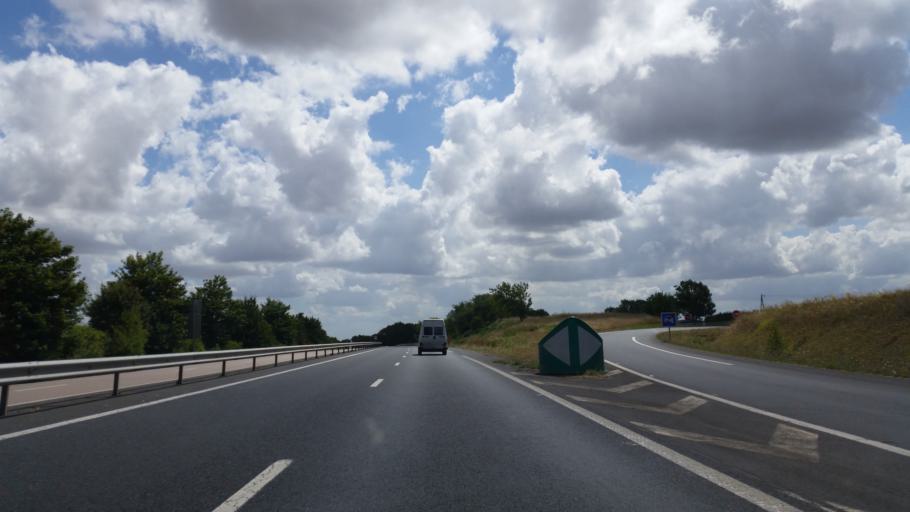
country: FR
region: Lower Normandy
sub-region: Departement du Calvados
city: Potigny
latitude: 48.9841
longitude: -0.2491
